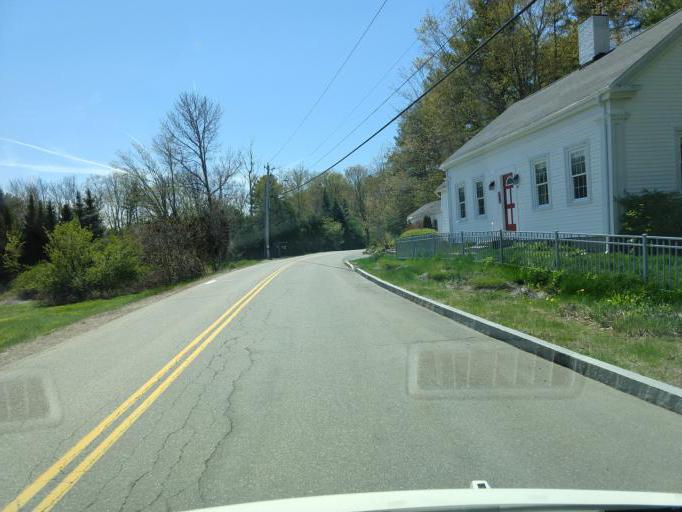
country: US
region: Maine
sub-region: York County
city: Ogunquit
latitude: 43.2389
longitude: -70.6116
